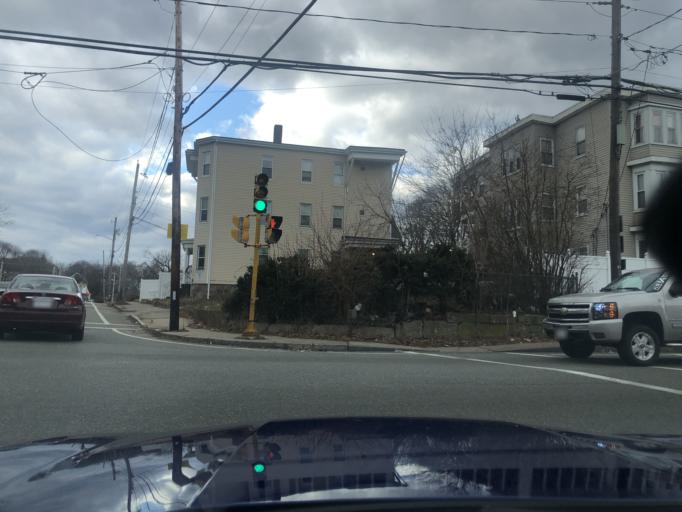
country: US
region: Massachusetts
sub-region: Plymouth County
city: Brockton
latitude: 42.0939
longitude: -71.0174
